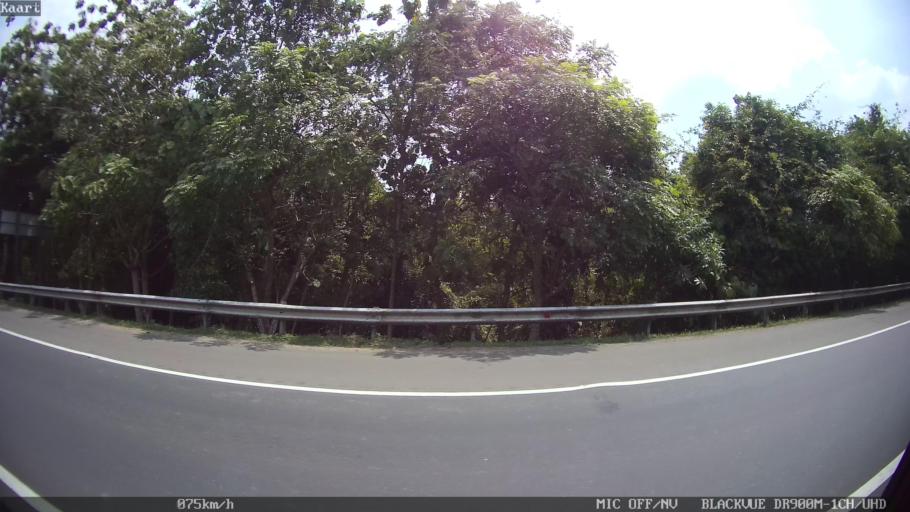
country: ID
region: Banten
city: Serang
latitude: -6.0772
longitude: 106.1315
